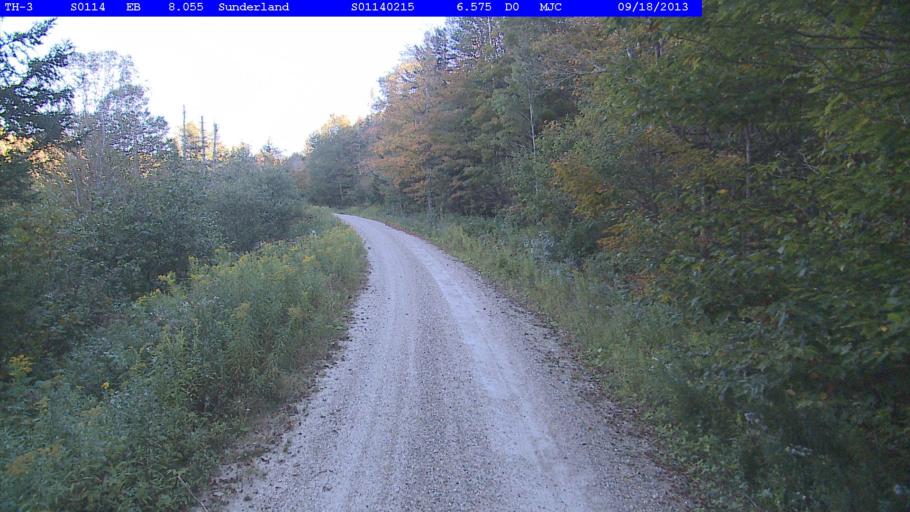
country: US
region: Vermont
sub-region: Bennington County
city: Arlington
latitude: 43.0537
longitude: -73.0571
